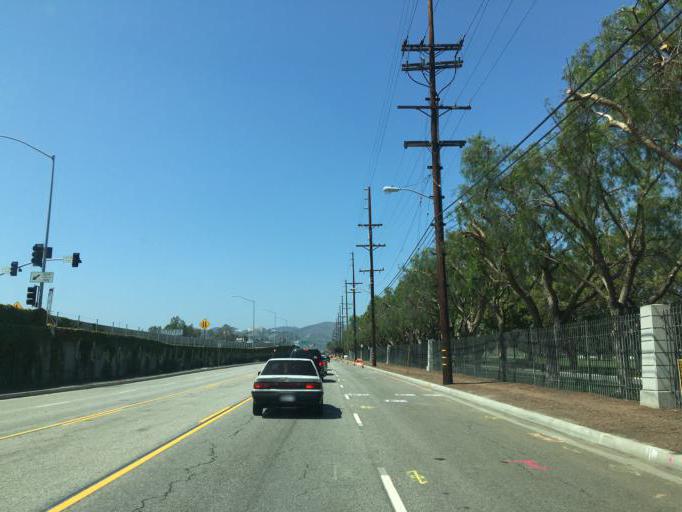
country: US
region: California
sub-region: Los Angeles County
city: Westwood, Los Angeles
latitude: 34.0578
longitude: -118.4530
